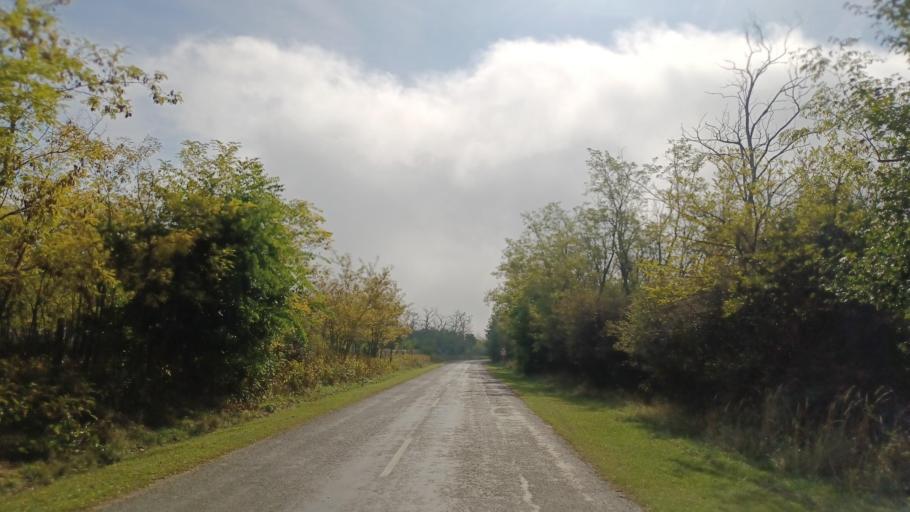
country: HU
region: Tolna
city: Pincehely
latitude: 46.6609
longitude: 18.4984
